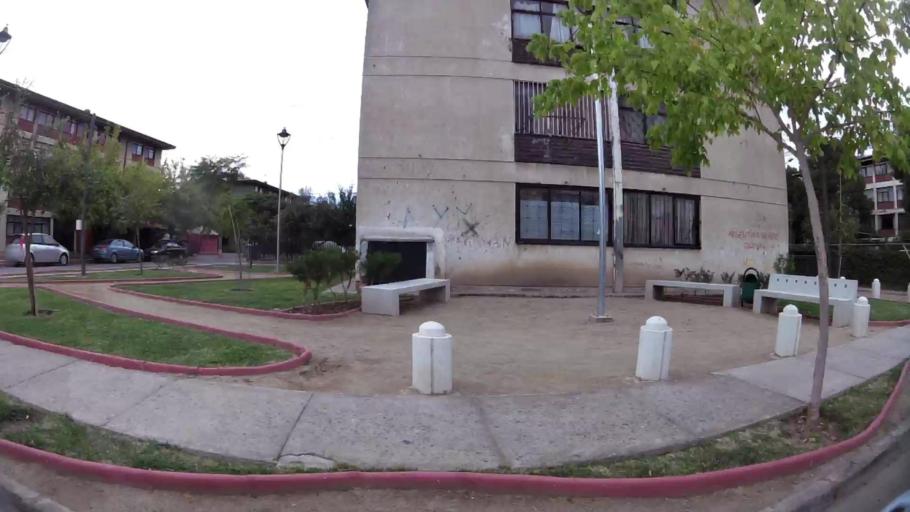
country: CL
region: O'Higgins
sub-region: Provincia de Cachapoal
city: Rancagua
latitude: -34.1478
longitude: -70.7406
